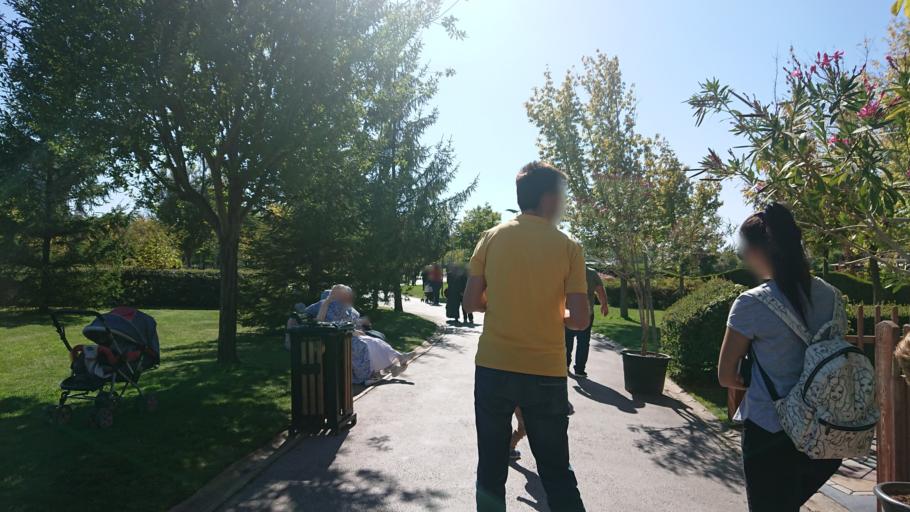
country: TR
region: Eskisehir
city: Eskisehir
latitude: 39.7627
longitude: 30.4738
